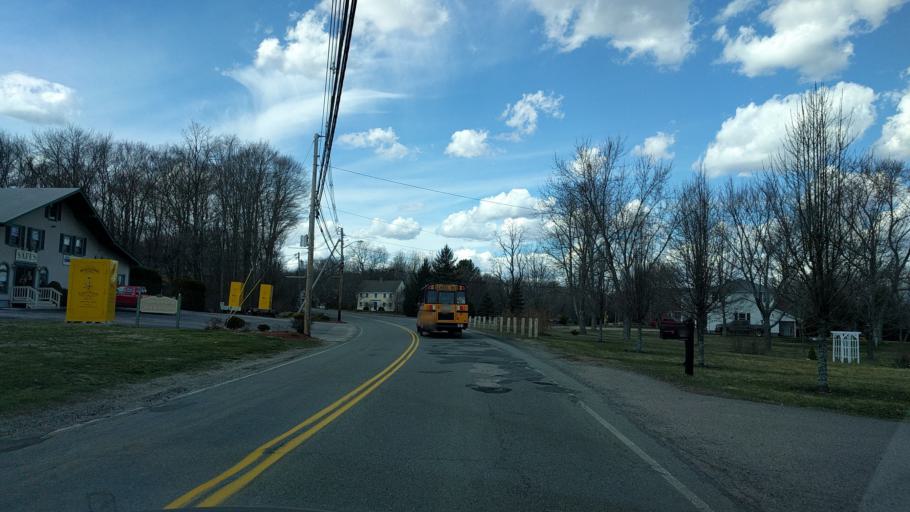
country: US
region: Massachusetts
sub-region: Worcester County
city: Mendon
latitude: 42.1012
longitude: -71.5426
